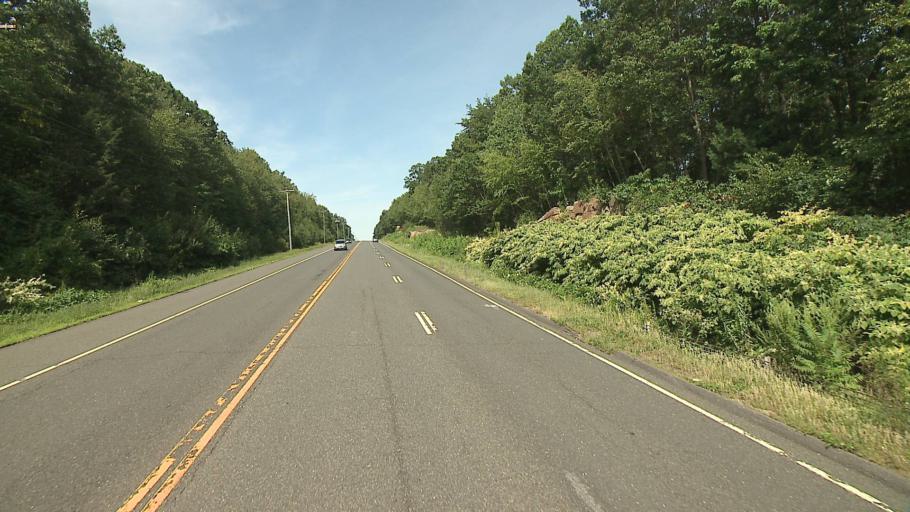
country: US
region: Connecticut
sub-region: Litchfield County
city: Oakville
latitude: 41.6043
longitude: -73.0781
